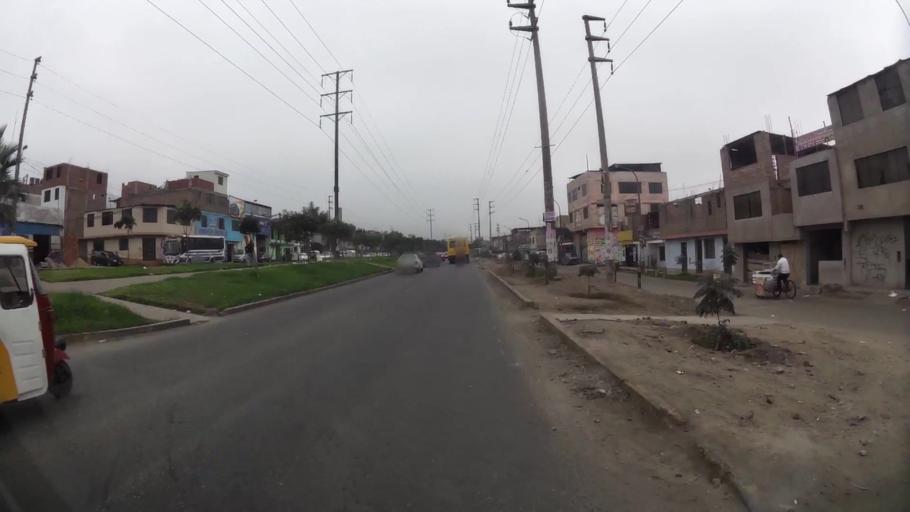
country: PE
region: Lima
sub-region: Lima
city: Surco
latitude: -12.1568
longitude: -76.9596
